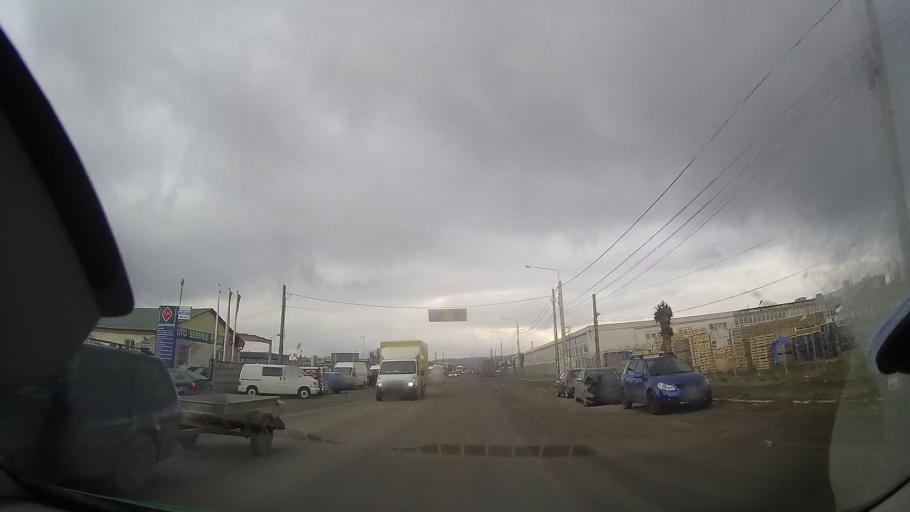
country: RO
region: Cluj
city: Turda
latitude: 46.5499
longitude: 23.7842
